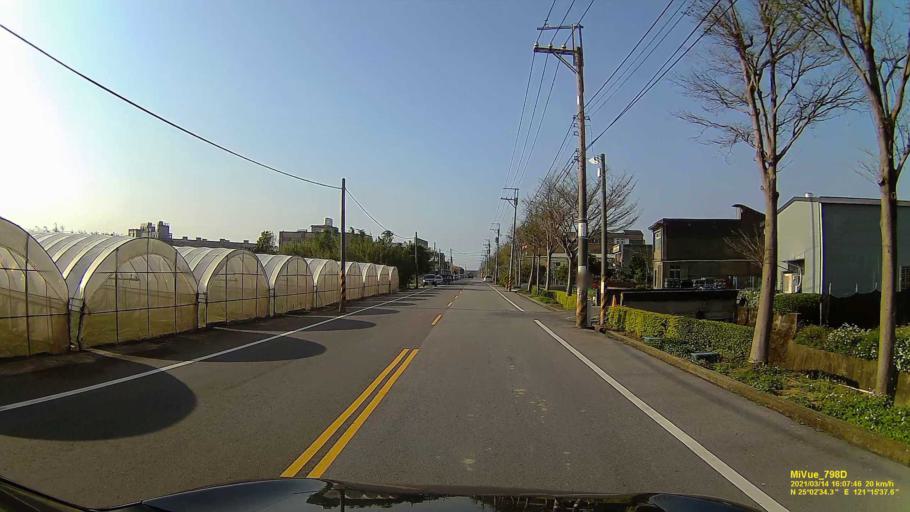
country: TW
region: Taiwan
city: Taoyuan City
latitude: 25.0429
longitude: 121.2604
